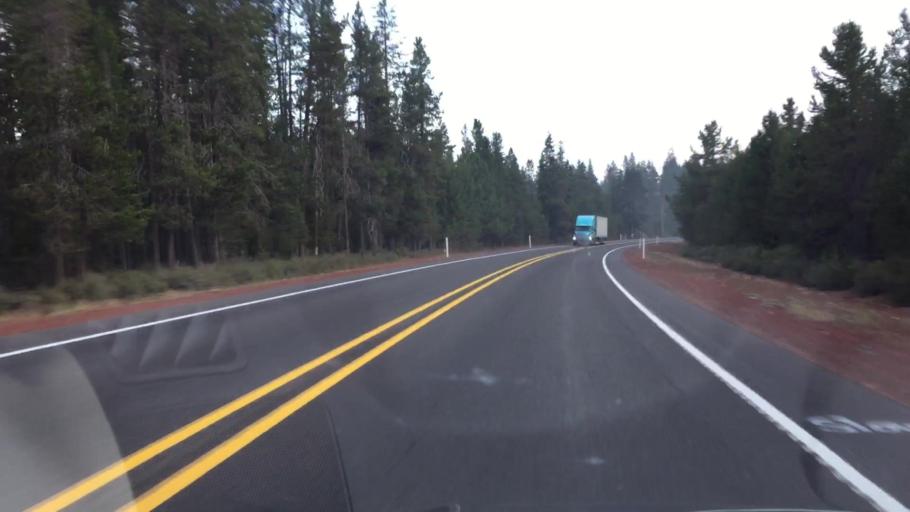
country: US
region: Oregon
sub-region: Deschutes County
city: La Pine
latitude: 43.3093
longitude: -121.7676
